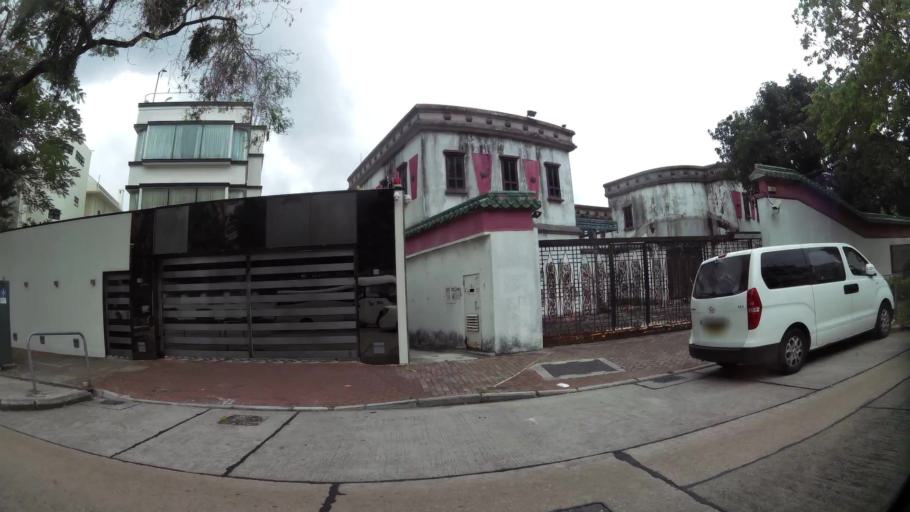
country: HK
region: Wong Tai Sin
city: Wong Tai Sin
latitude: 22.3401
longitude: 114.1765
